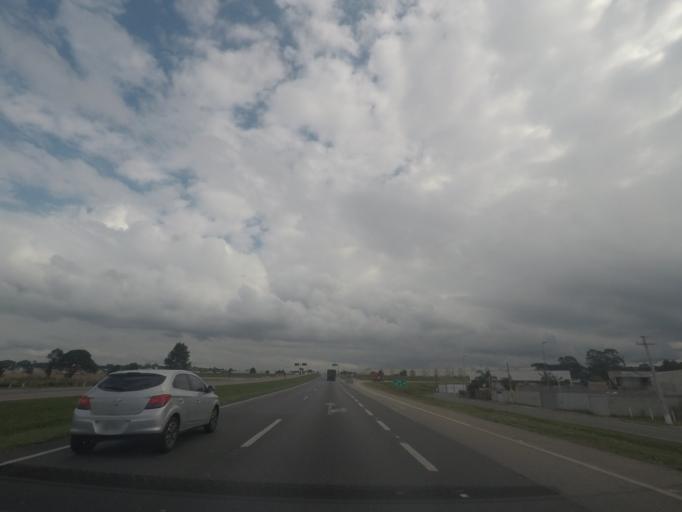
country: BR
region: Parana
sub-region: Sao Jose Dos Pinhais
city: Sao Jose dos Pinhais
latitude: -25.5078
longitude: -49.1254
